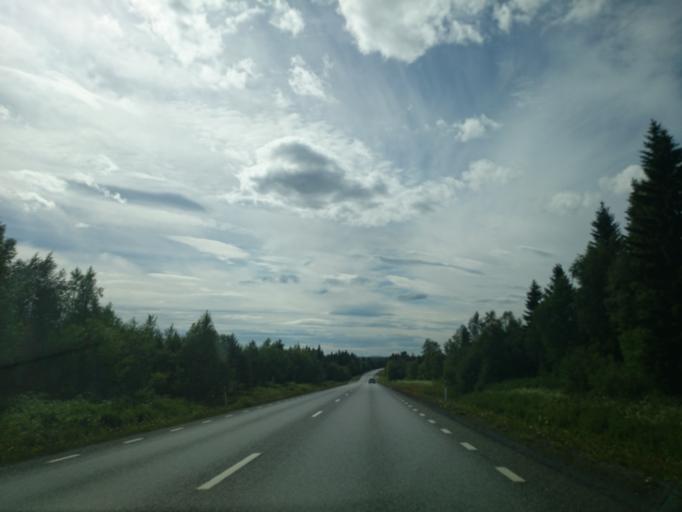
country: SE
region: Jaemtland
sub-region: Krokoms Kommun
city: Valla
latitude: 63.3063
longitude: 13.8496
